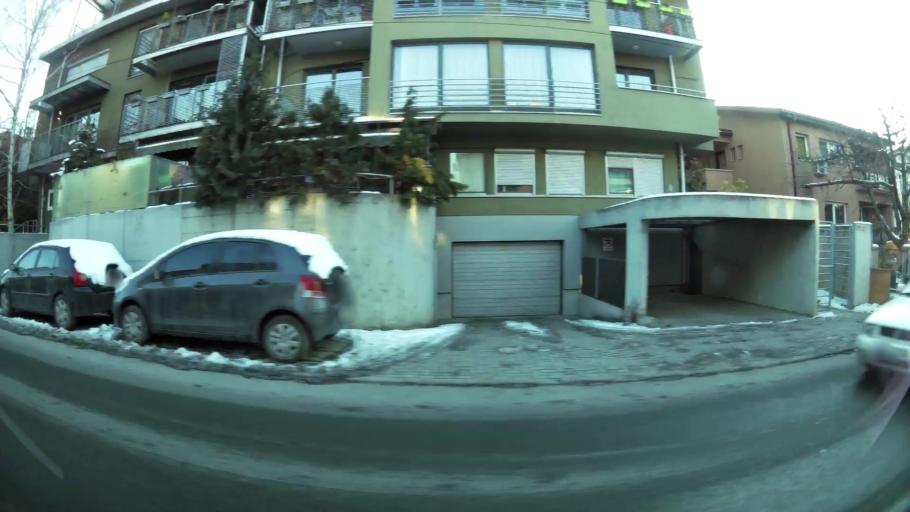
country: MK
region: Karpos
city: Skopje
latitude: 41.9962
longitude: 21.3915
